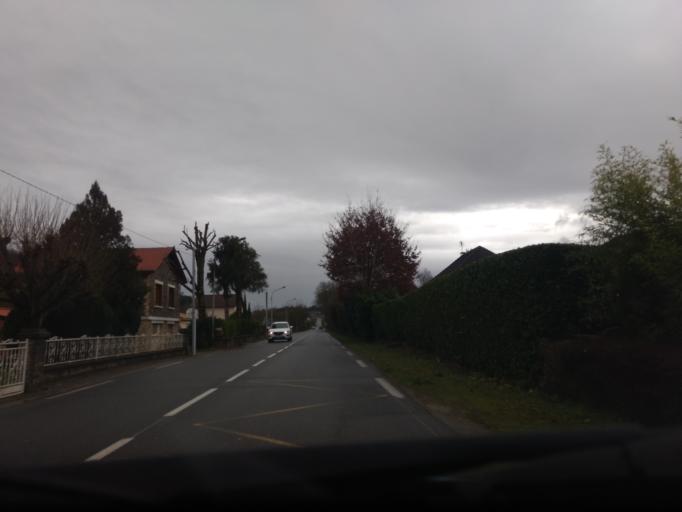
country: FR
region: Midi-Pyrenees
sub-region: Departement de l'Aveyron
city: Firmi
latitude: 44.5284
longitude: 2.3269
